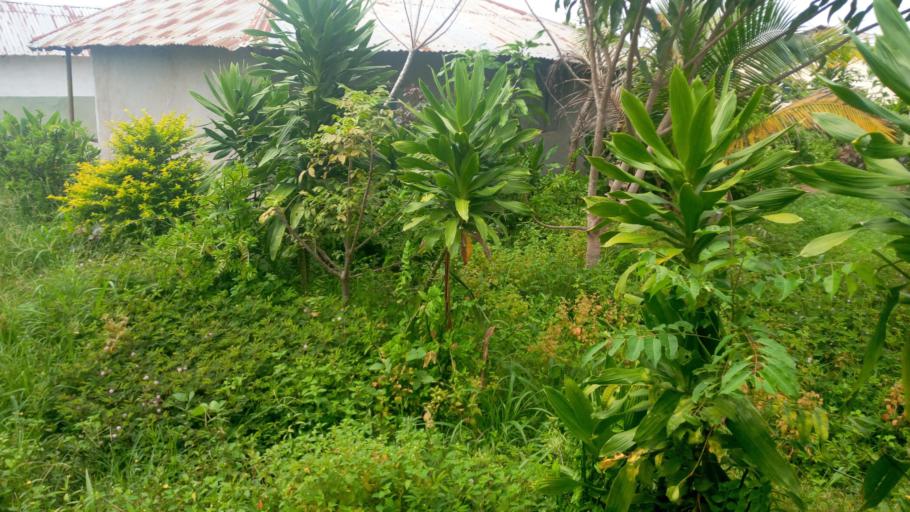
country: SL
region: Southern Province
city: Mogbwemo
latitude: 7.7748
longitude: -12.3018
